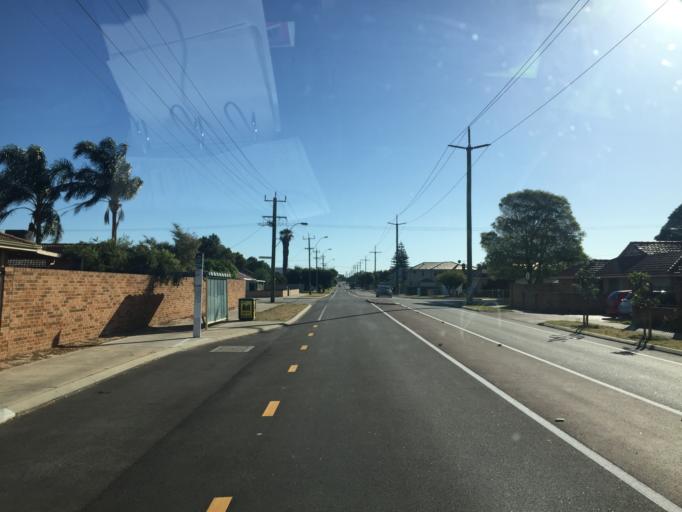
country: AU
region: Western Australia
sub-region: Belmont
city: Rivervale
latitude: -31.9623
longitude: 115.9270
